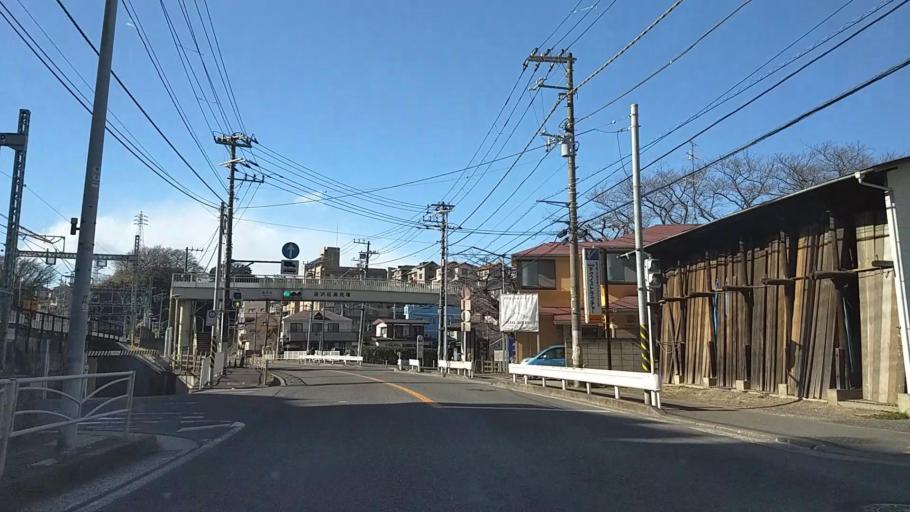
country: JP
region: Kanagawa
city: Yokohama
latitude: 35.3737
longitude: 139.6267
